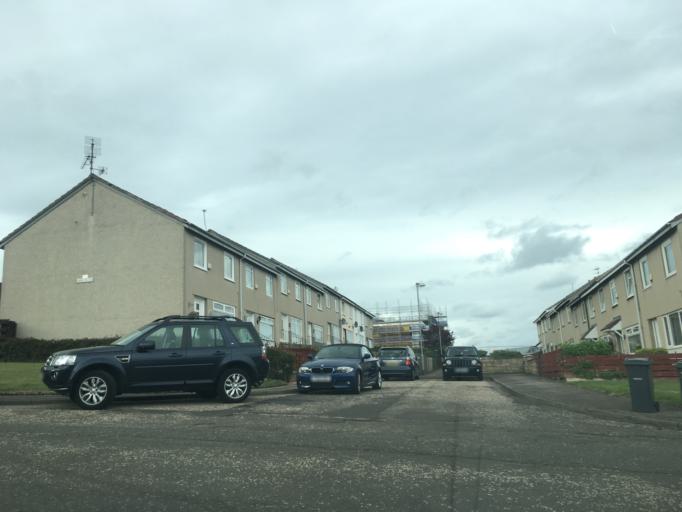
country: GB
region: Scotland
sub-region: Edinburgh
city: Colinton
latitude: 55.9261
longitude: -3.2660
